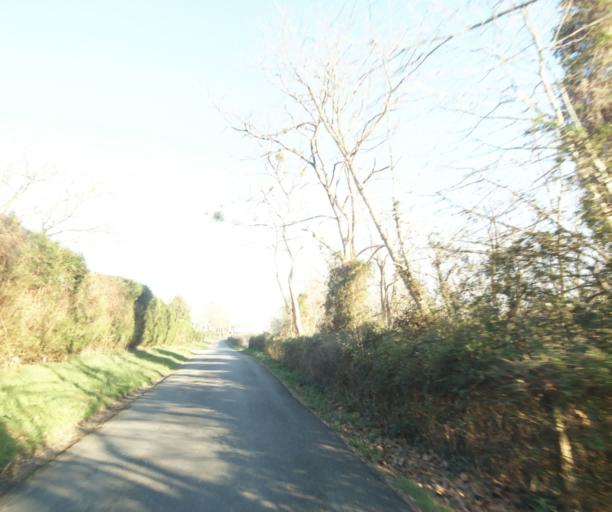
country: FR
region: Aquitaine
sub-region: Departement des Pyrenees-Atlantiques
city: Urrugne
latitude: 43.3473
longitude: -1.7052
